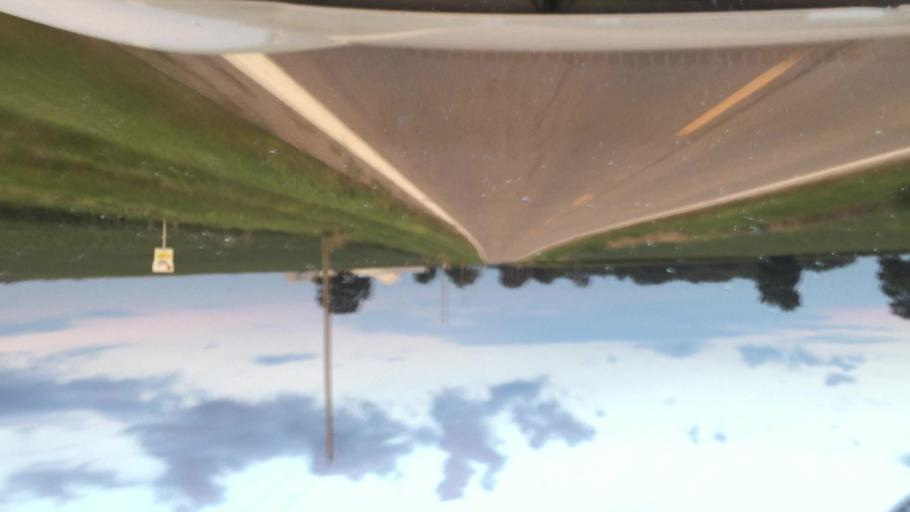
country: US
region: Ohio
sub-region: Madison County
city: Choctaw Lake
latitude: 40.0293
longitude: -83.4867
